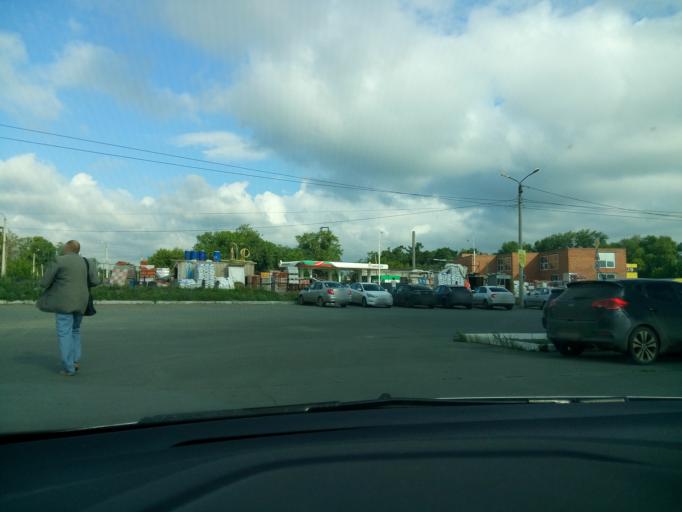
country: RU
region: Chelyabinsk
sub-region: Gorod Chelyabinsk
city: Chelyabinsk
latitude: 55.2347
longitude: 61.3674
